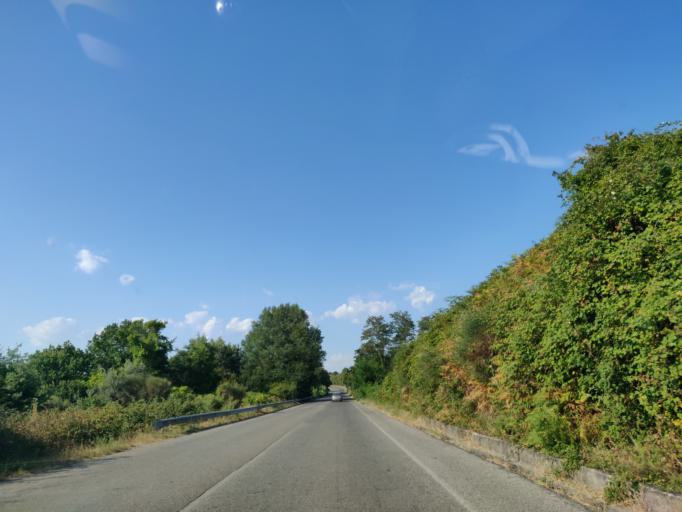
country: IT
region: Latium
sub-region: Provincia di Viterbo
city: Valentano
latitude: 42.5832
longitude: 11.8332
